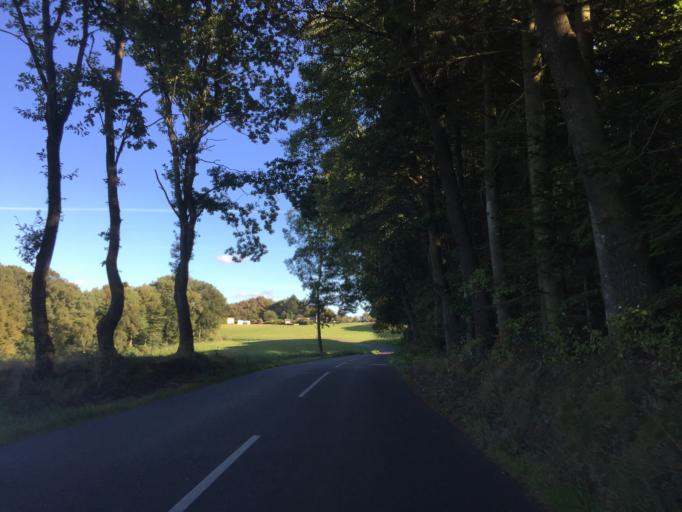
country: DK
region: Central Jutland
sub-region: Silkeborg Kommune
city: Svejbaek
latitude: 56.2223
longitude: 9.6927
